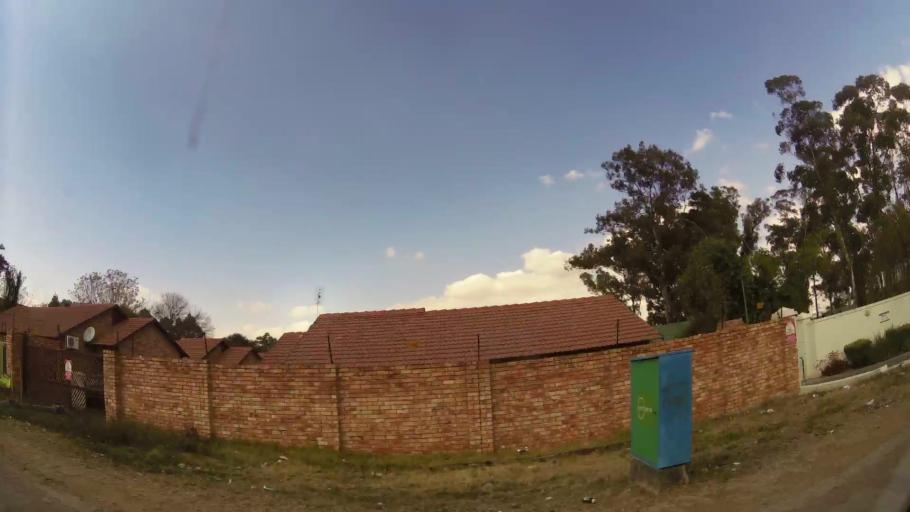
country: ZA
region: Gauteng
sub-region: City of Johannesburg Metropolitan Municipality
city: Midrand
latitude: -25.9940
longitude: 28.1109
